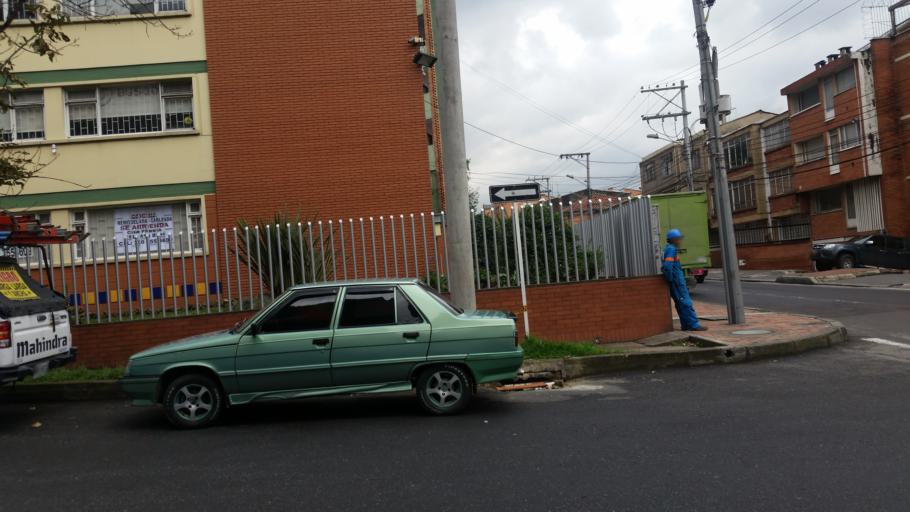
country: CO
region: Bogota D.C.
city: Barrio San Luis
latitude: 4.6502
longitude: -74.0555
